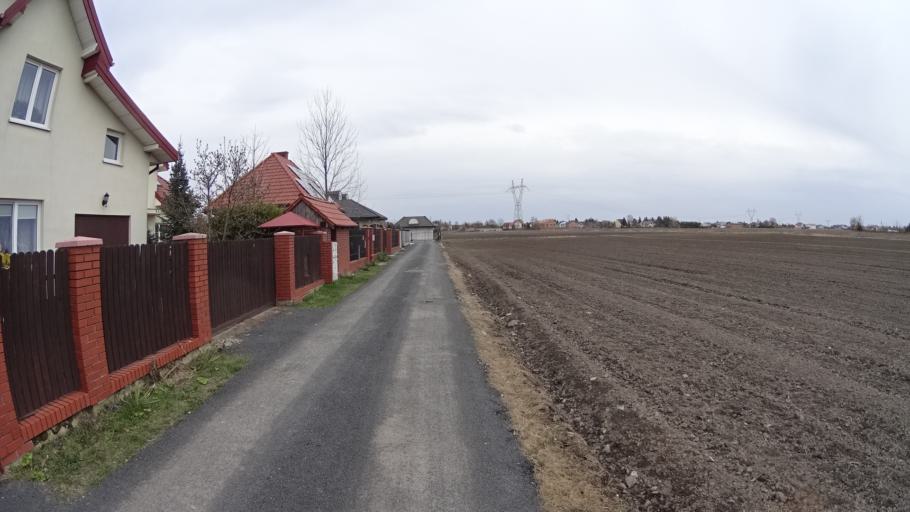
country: PL
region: Masovian Voivodeship
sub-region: Powiat warszawski zachodni
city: Stare Babice
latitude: 52.2489
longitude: 20.8262
